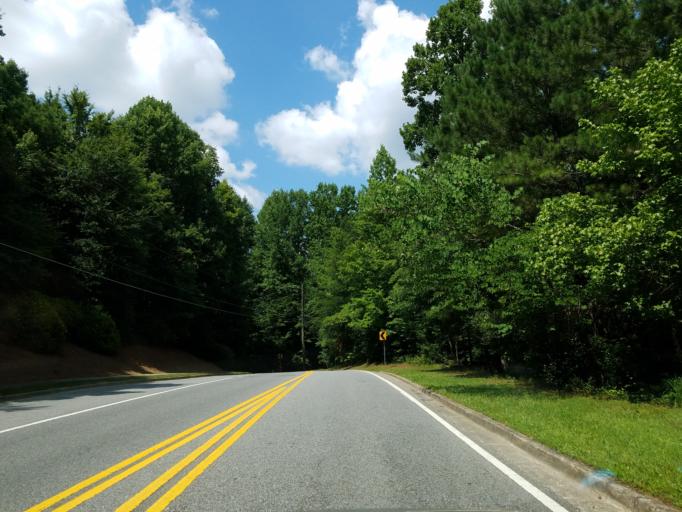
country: US
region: Georgia
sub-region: Fulton County
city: Roswell
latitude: 34.0002
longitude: -84.3338
